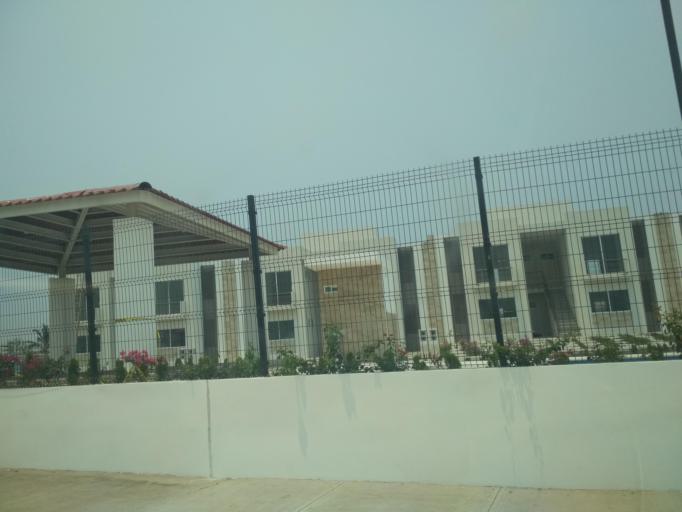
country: MX
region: Veracruz
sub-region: Veracruz
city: Las Amapolas
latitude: 19.1503
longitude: -96.2053
